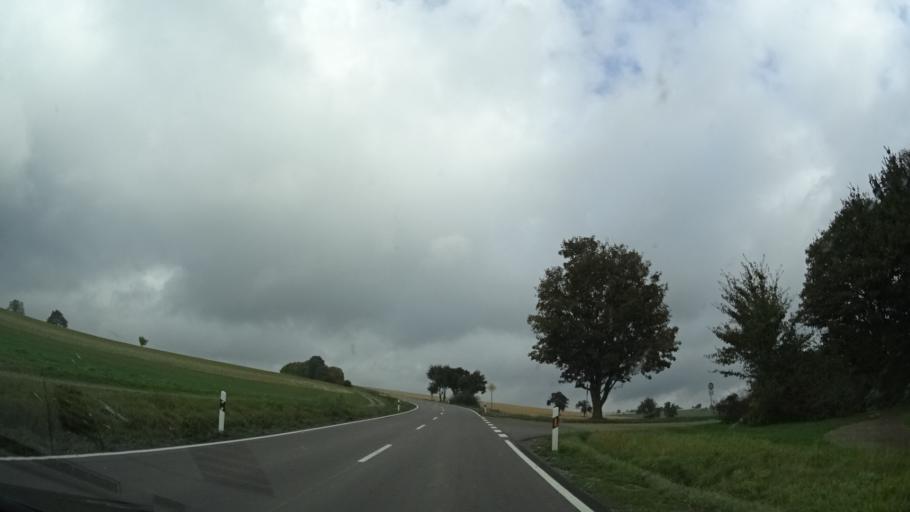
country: DE
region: Baden-Wuerttemberg
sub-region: Karlsruhe Region
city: Konigsbach-Stein
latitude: 48.9744
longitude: 8.6372
